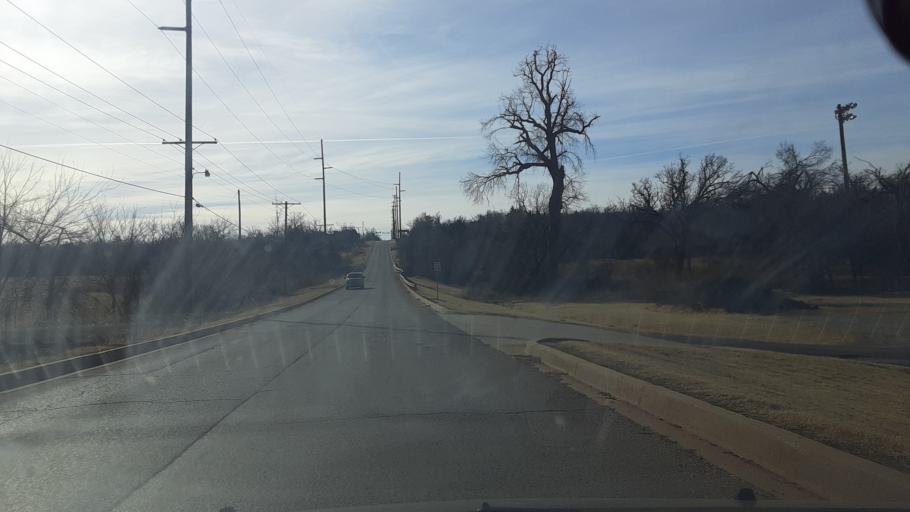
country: US
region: Oklahoma
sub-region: Logan County
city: Guthrie
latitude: 35.8850
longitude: -97.4075
